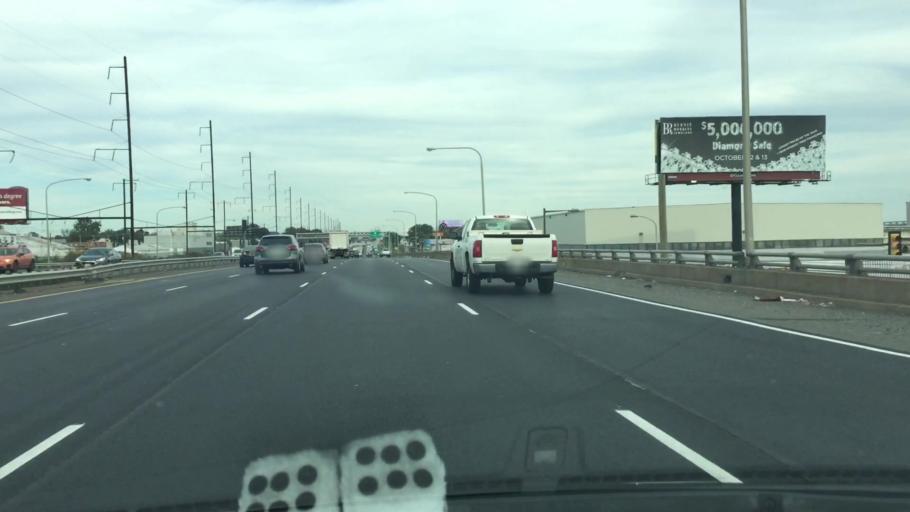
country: US
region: New Jersey
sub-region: Burlington County
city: Palmyra
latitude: 40.0140
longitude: -75.0558
